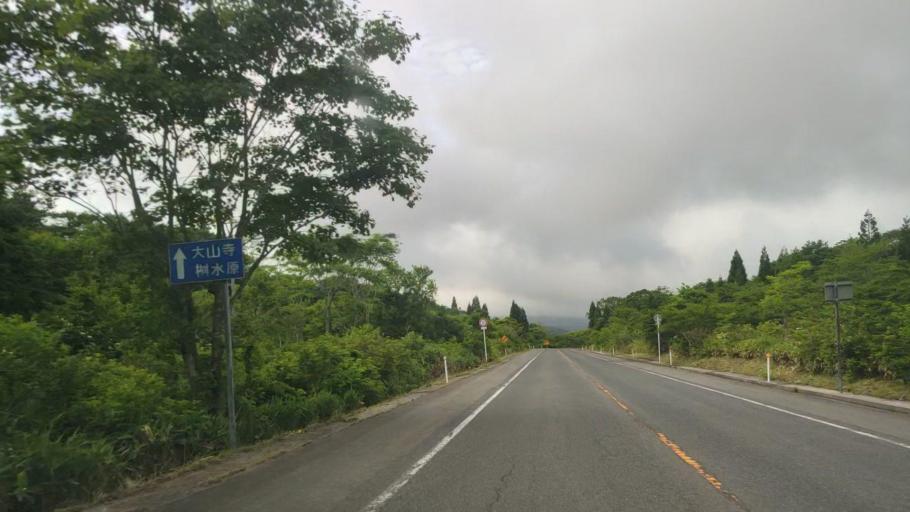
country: JP
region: Tottori
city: Kurayoshi
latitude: 35.3357
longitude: 133.5804
